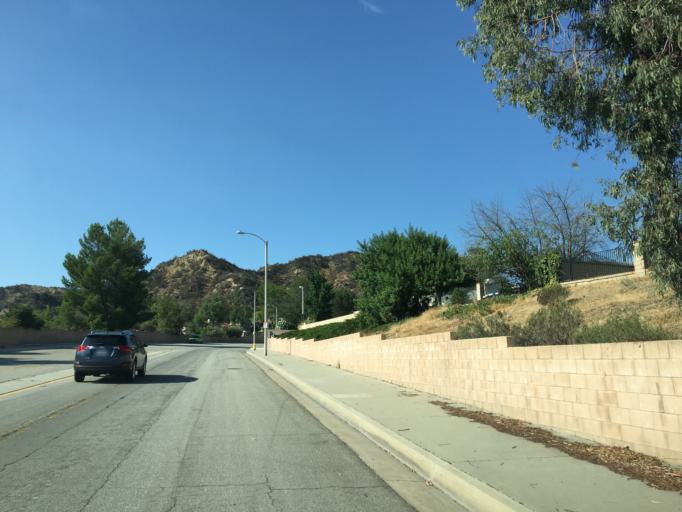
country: US
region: California
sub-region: Los Angeles County
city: Castaic
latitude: 34.4918
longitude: -118.6278
